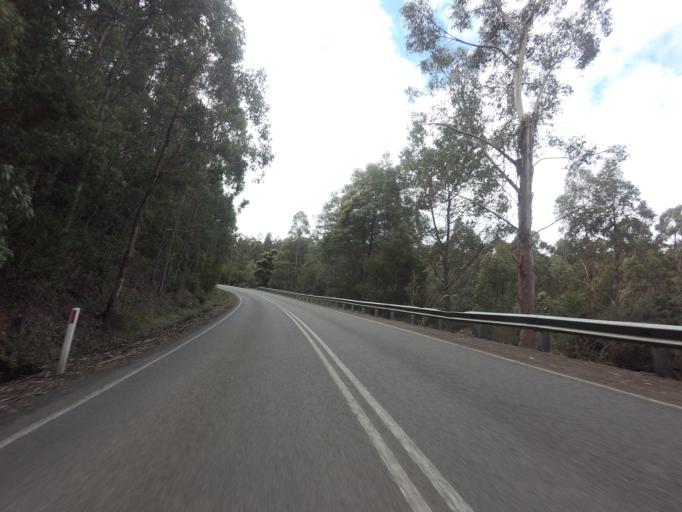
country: AU
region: Tasmania
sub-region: Huon Valley
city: Geeveston
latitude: -43.4093
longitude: 146.9588
